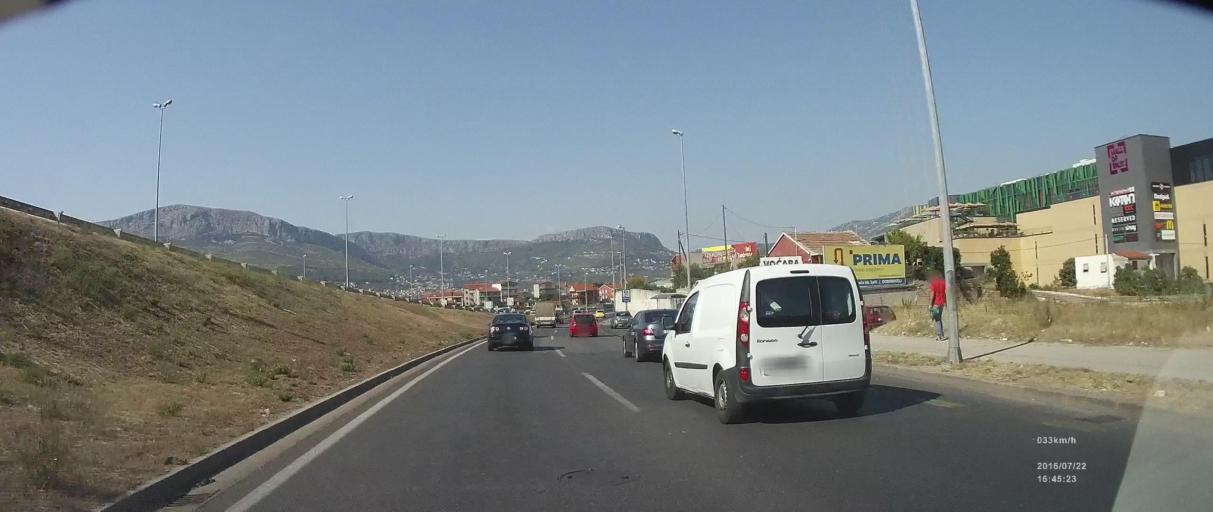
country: HR
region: Splitsko-Dalmatinska
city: Vranjic
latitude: 43.5187
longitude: 16.4814
